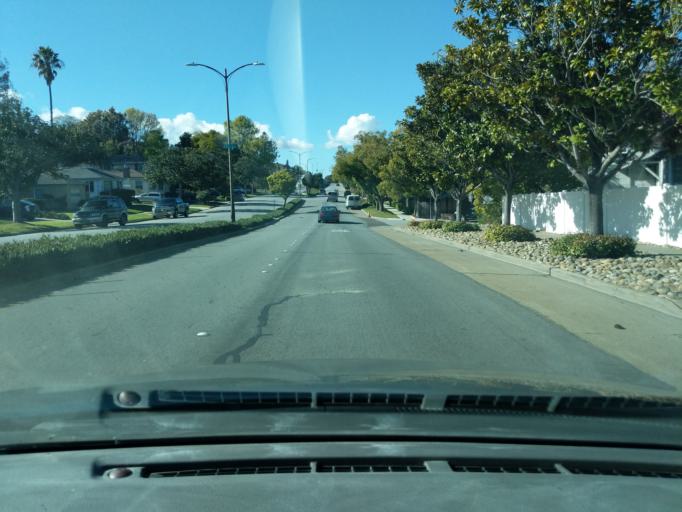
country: US
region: California
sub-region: San Mateo County
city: San Mateo
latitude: 37.5415
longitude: -122.3155
